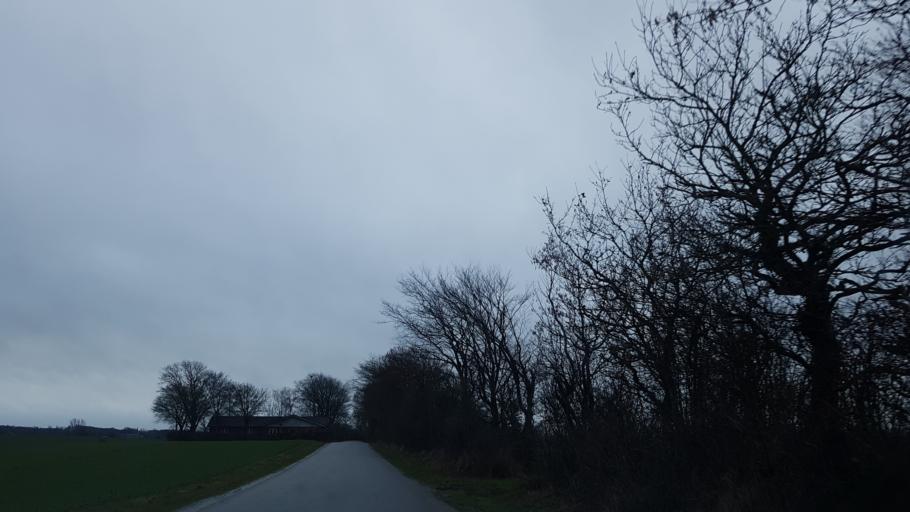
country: DK
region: South Denmark
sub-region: Kolding Kommune
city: Vamdrup
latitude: 55.3869
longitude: 9.3021
